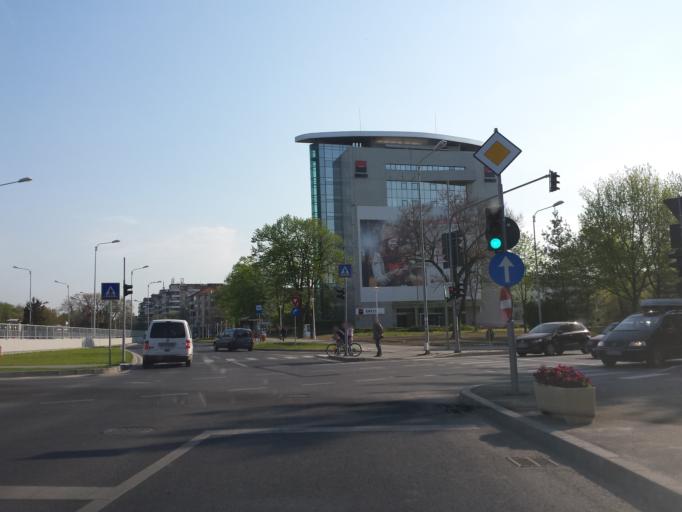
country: RO
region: Timis
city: Timisoara
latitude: 45.7489
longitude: 21.2364
